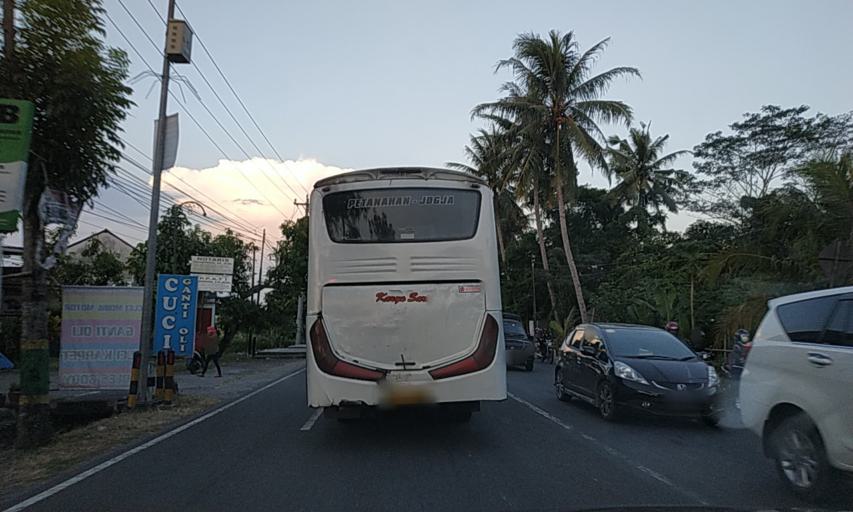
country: ID
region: Daerah Istimewa Yogyakarta
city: Srandakan
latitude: -7.8706
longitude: 110.1423
